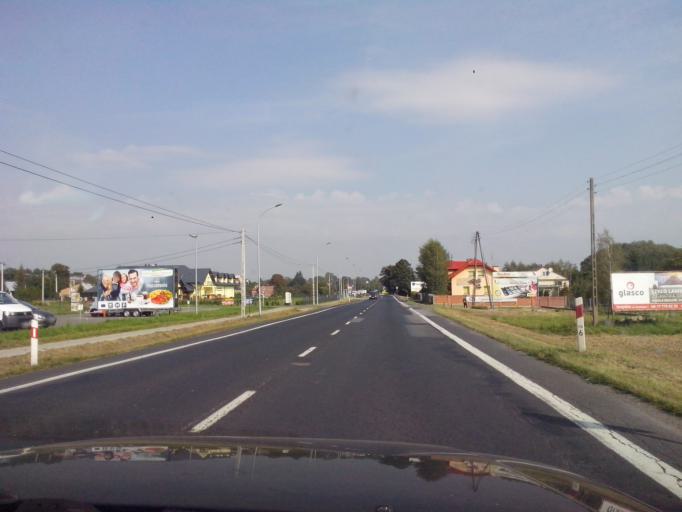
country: PL
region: Subcarpathian Voivodeship
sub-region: Powiat rzeszowski
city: Lutoryz
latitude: 49.9553
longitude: 21.9156
